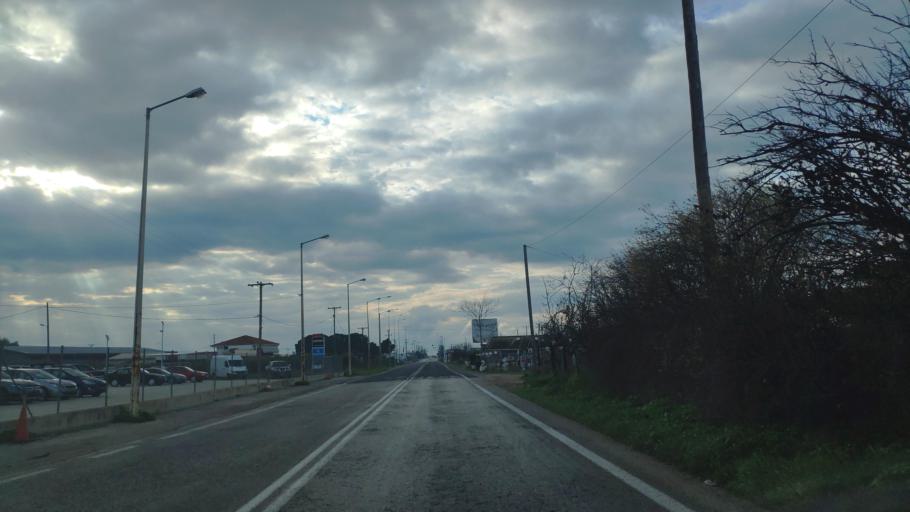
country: GR
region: Peloponnese
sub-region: Nomos Argolidos
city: Argos
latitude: 37.6562
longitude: 22.7268
